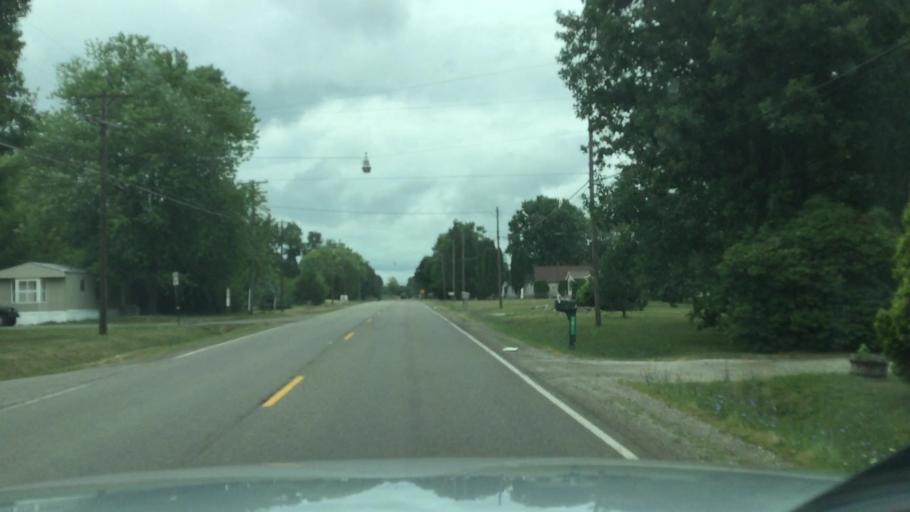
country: US
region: Michigan
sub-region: Genesee County
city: Beecher
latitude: 43.0794
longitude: -83.6366
